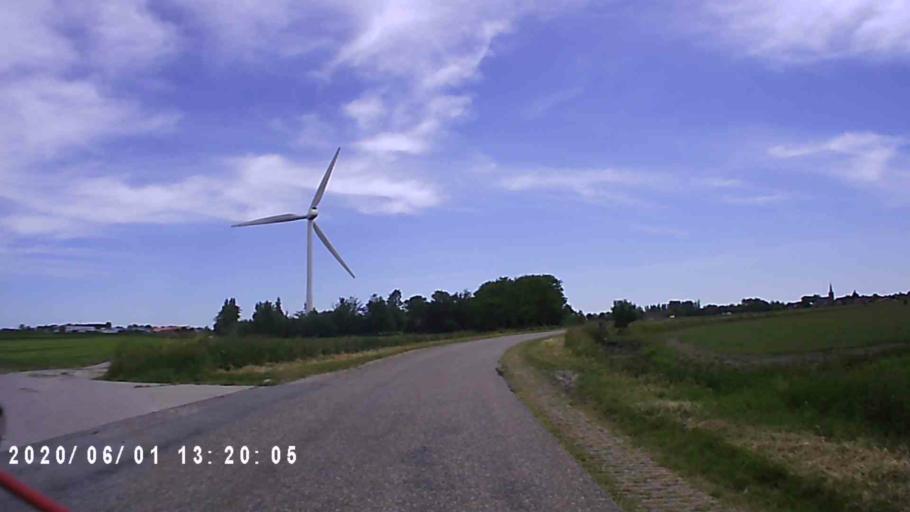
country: NL
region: Friesland
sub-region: Gemeente Littenseradiel
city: Wommels
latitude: 53.1150
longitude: 5.5823
